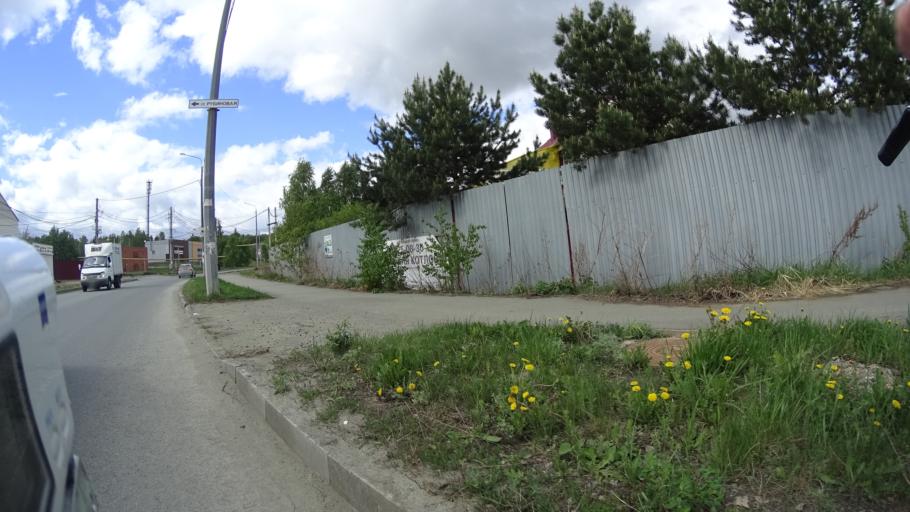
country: RU
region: Chelyabinsk
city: Sargazy
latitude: 55.1529
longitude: 61.2552
